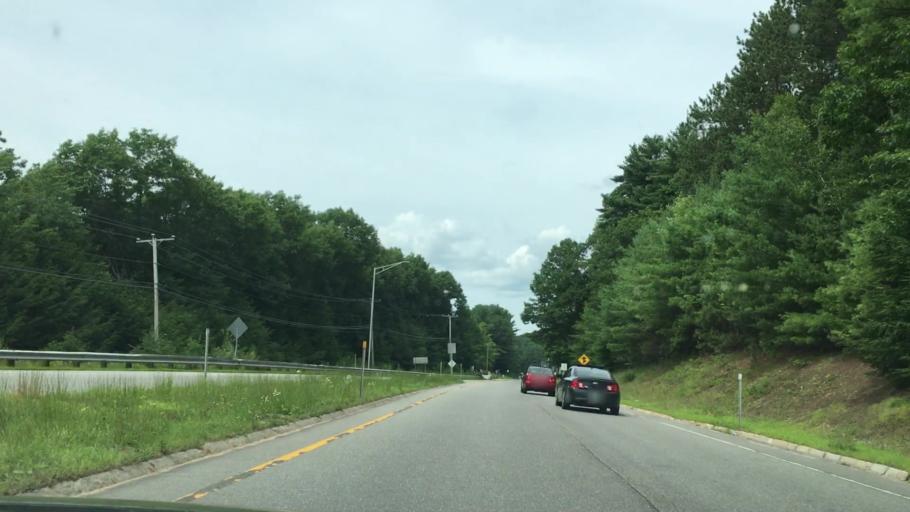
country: US
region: New Hampshire
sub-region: Cheshire County
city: Rindge
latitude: 42.7635
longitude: -72.0376
